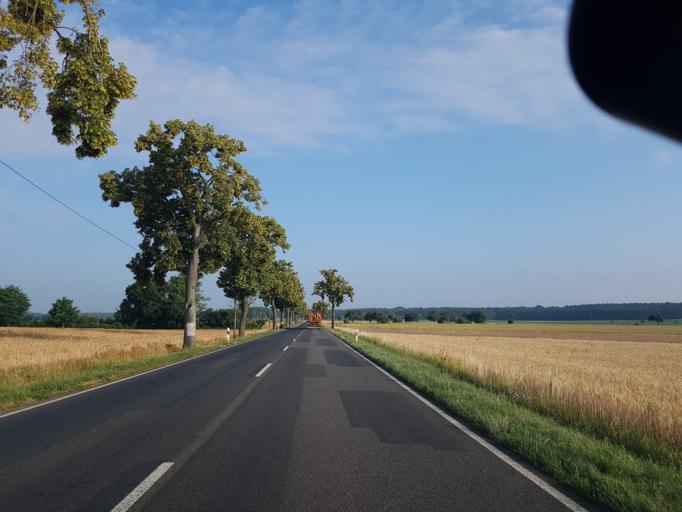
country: DE
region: Brandenburg
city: Schlieben
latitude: 51.7265
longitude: 13.3698
